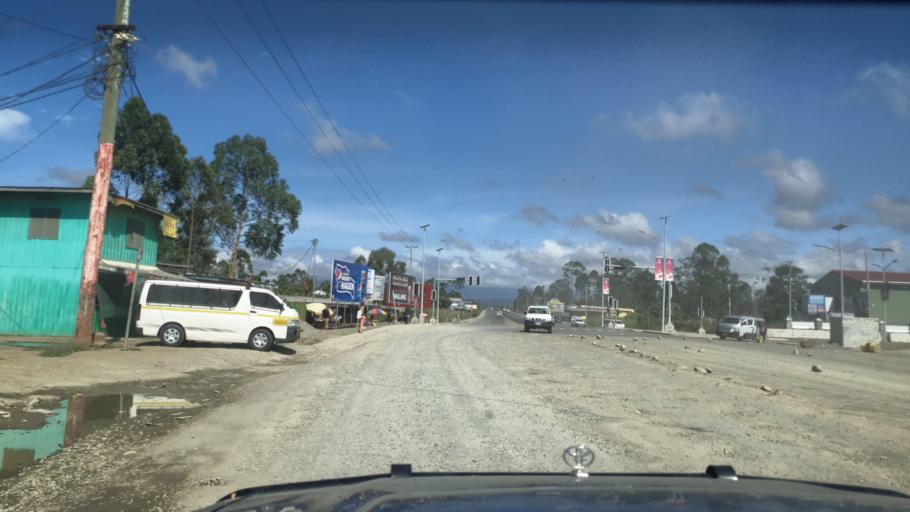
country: PG
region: Western Highlands
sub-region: Hagen
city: Mount Hagen
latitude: -5.8406
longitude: 144.3002
